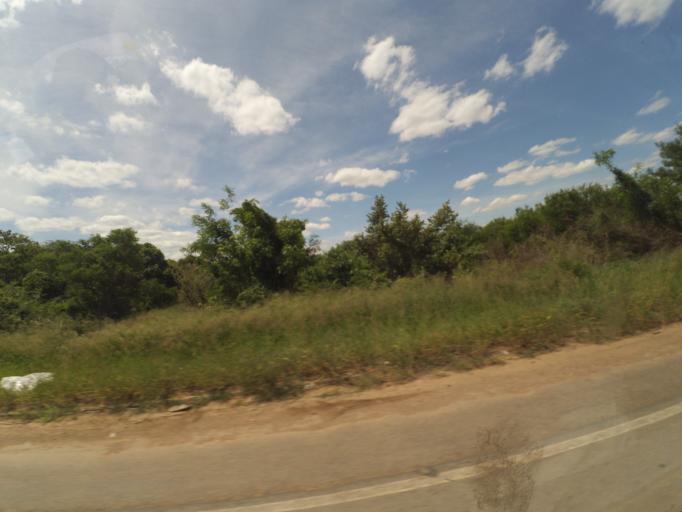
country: BO
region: Santa Cruz
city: Pailon
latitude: -17.5919
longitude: -61.9874
